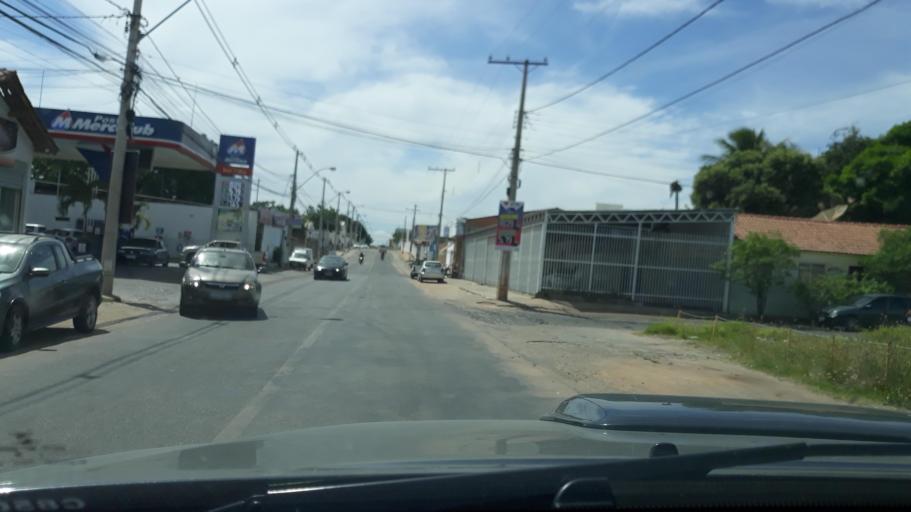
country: BR
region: Bahia
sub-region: Guanambi
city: Guanambi
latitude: -14.2146
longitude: -42.7722
